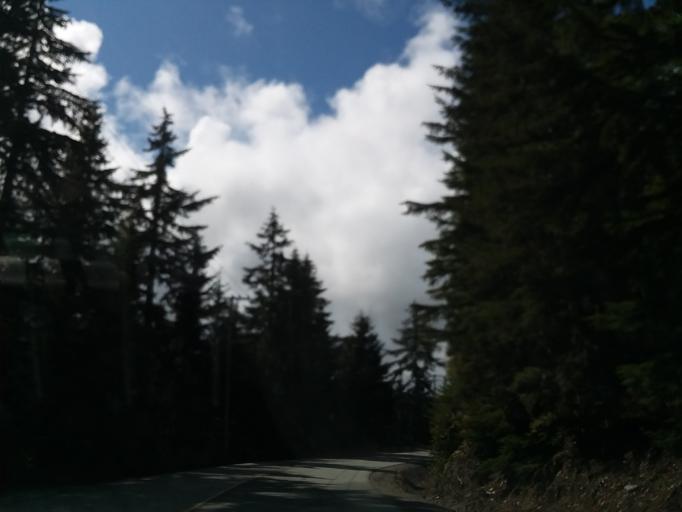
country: CA
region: British Columbia
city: Whistler
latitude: 50.1038
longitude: -122.9939
